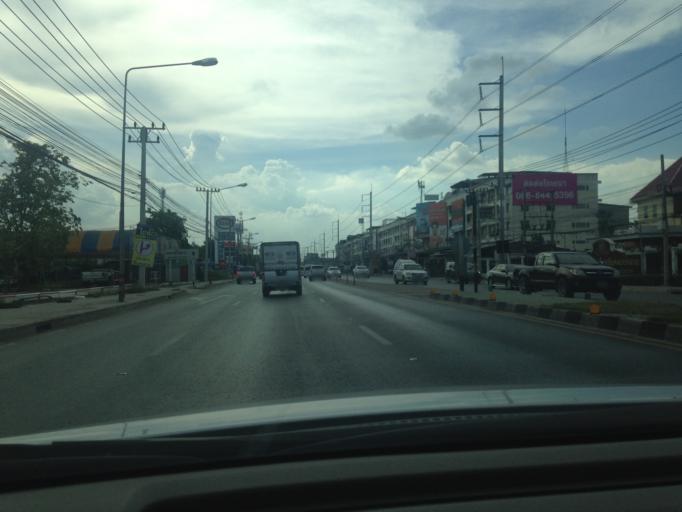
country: TH
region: Pathum Thani
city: Khlong Luang
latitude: 14.0656
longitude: 100.6524
